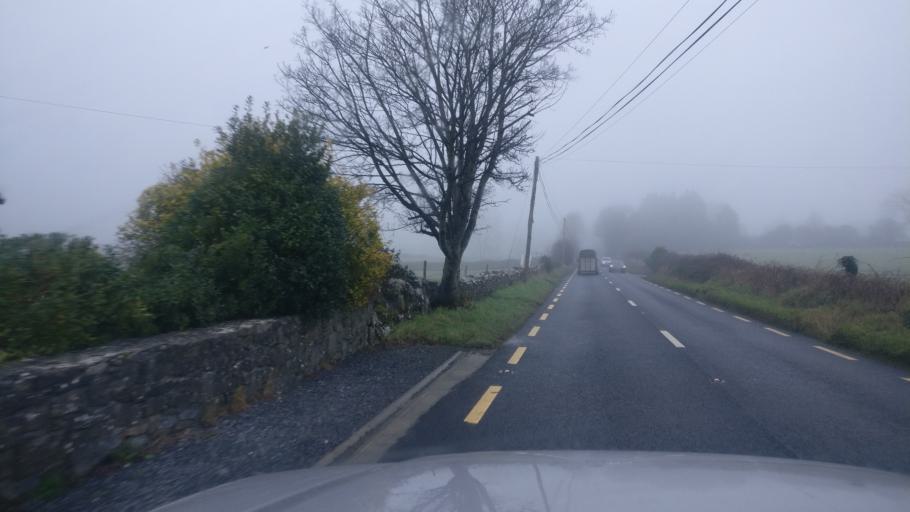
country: IE
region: Connaught
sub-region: County Galway
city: Loughrea
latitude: 53.1757
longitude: -8.6578
